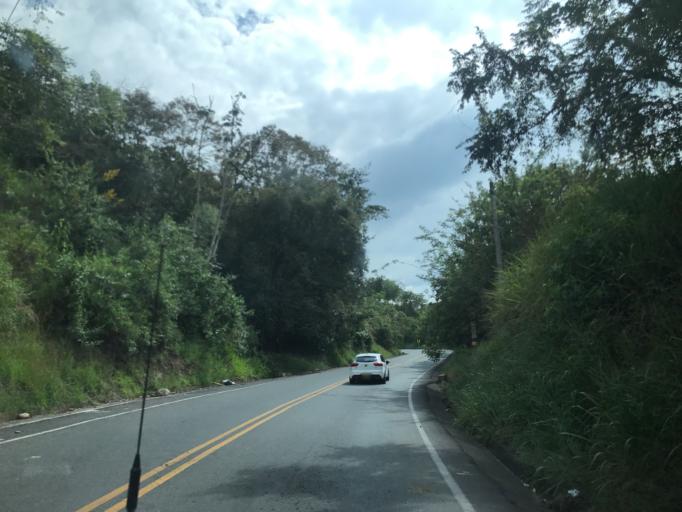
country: CO
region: Valle del Cauca
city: Cartago
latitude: 4.7359
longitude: -75.8959
